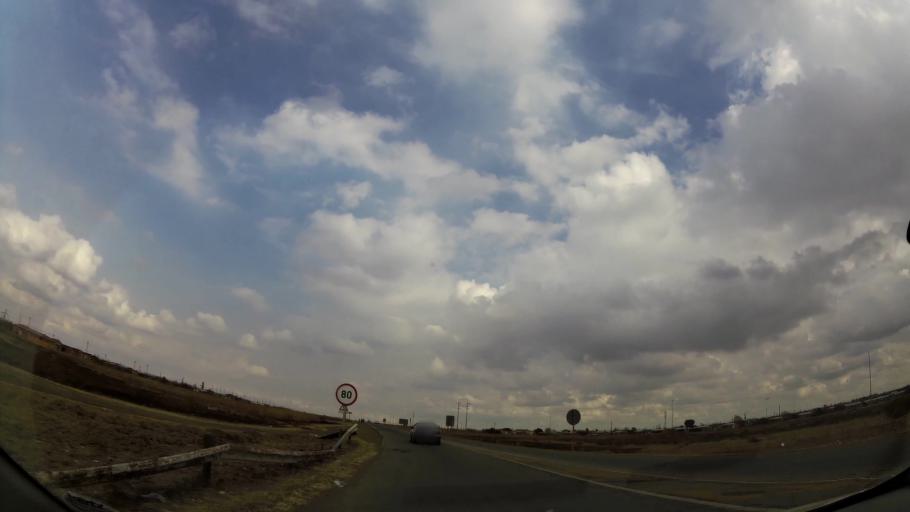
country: ZA
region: Orange Free State
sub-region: Fezile Dabi District Municipality
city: Sasolburg
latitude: -26.8476
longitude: 27.8895
